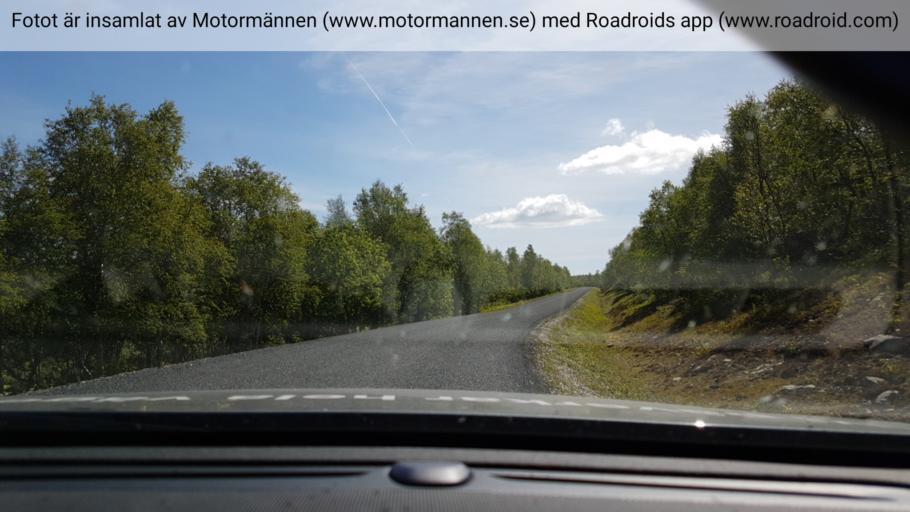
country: NO
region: Nordland
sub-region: Hattfjelldal
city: Hattfjelldal
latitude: 65.4237
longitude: 14.9025
